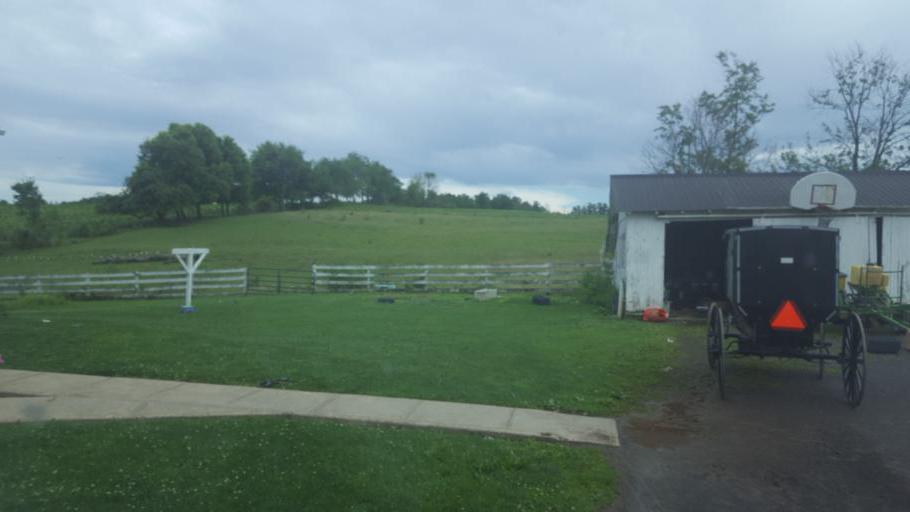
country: US
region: Ohio
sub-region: Knox County
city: Fredericktown
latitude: 40.4963
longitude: -82.6311
